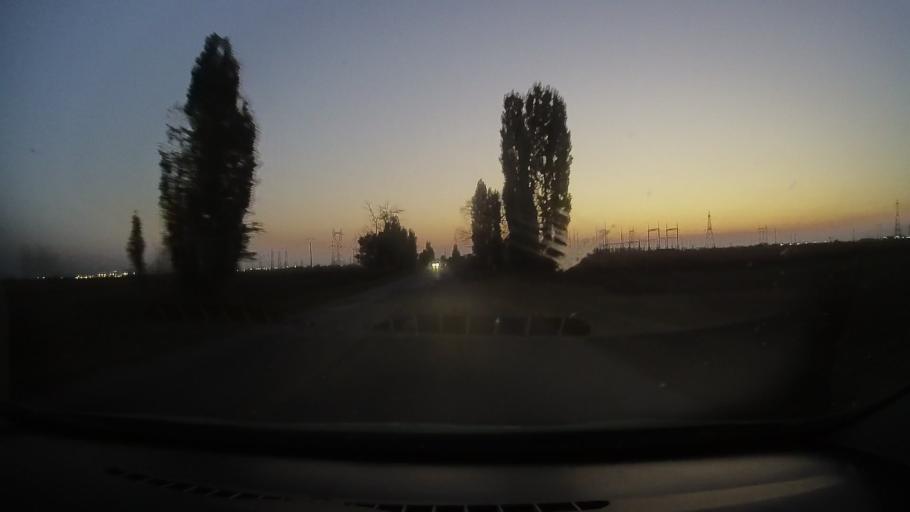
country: RO
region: Arad
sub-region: Comuna Vladimirescu
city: Vladimirescu
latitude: 46.1856
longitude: 21.3851
